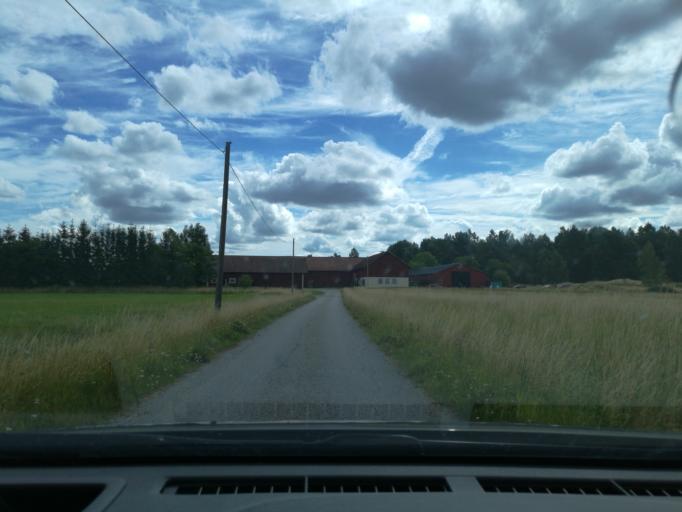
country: SE
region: Stockholm
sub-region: Sigtuna Kommun
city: Marsta
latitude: 59.6474
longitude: 17.8987
